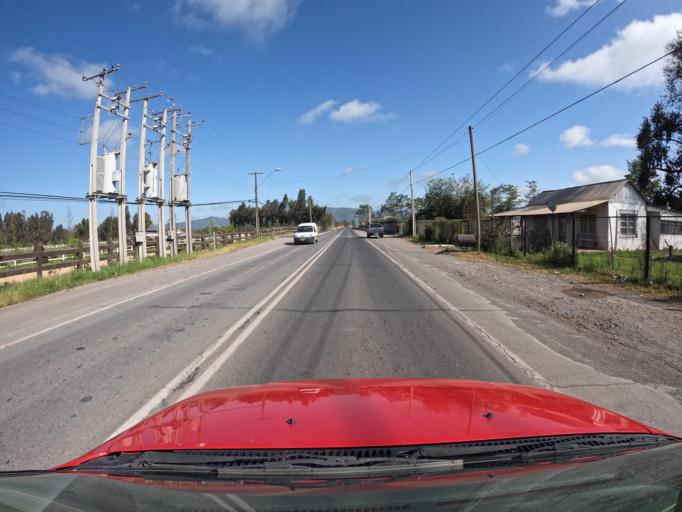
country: CL
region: Maule
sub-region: Provincia de Curico
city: Rauco
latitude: -34.9359
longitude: -71.2709
